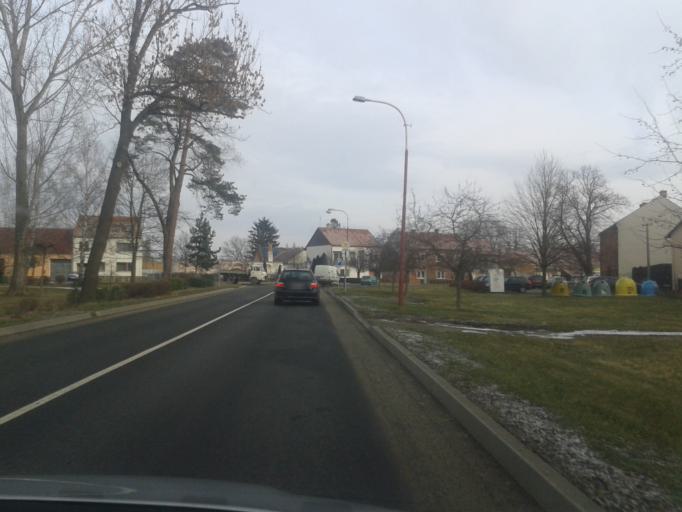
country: CZ
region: Olomoucky
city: Smrzice
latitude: 49.5060
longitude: 17.1021
